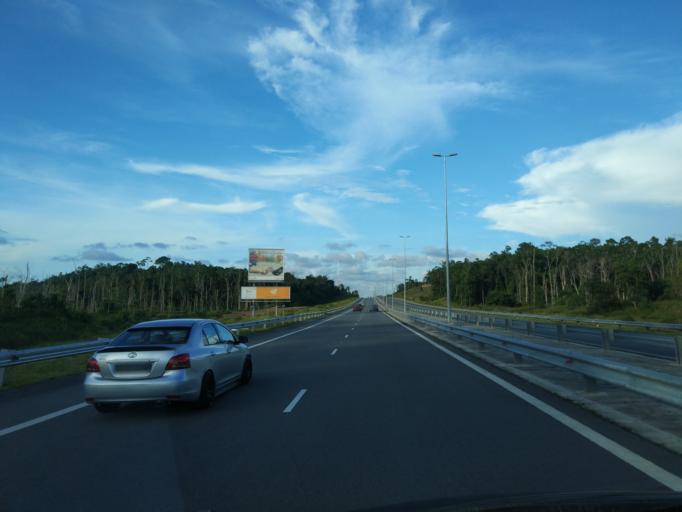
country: BN
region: Tutong
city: Tutong
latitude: 4.6786
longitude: 114.5397
